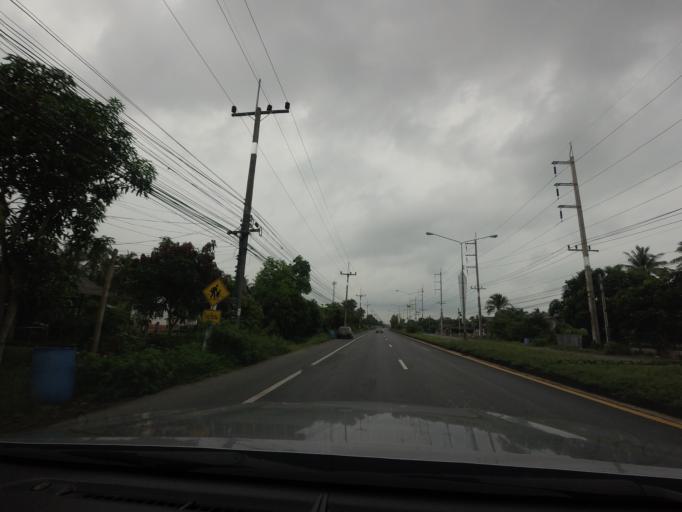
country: TH
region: Songkhla
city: Sathing Phra
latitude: 7.3878
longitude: 100.4696
